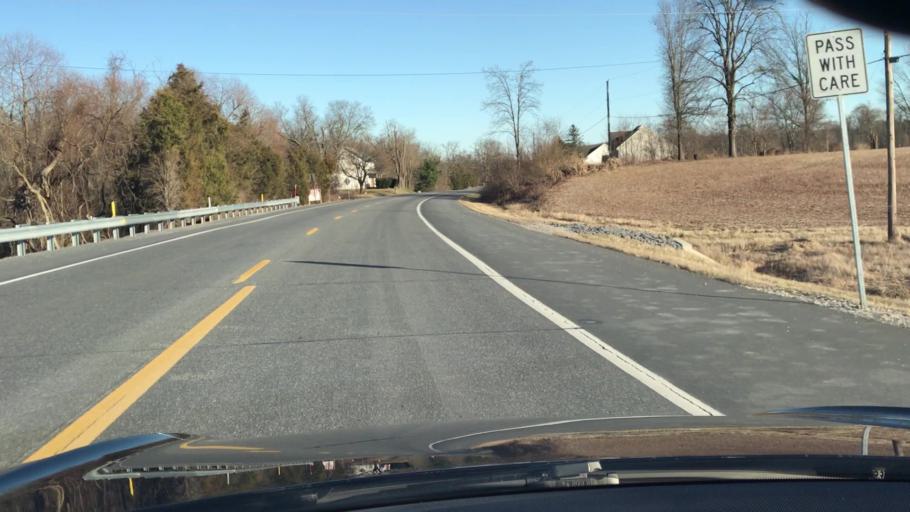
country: US
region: Pennsylvania
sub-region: Cumberland County
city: Lower Allen
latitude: 40.1454
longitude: -76.8773
